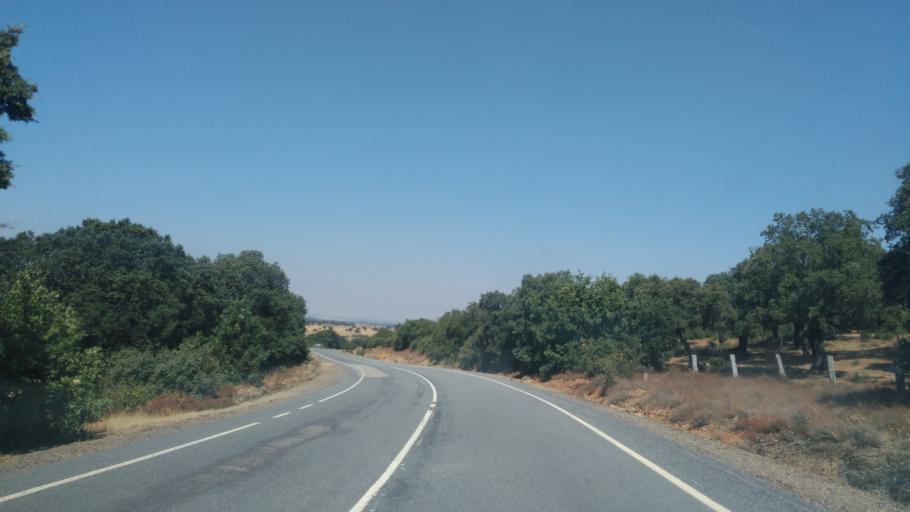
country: ES
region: Castille and Leon
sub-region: Provincia de Salamanca
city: Aldeanueva de la Sierra
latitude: 40.6073
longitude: -6.0950
